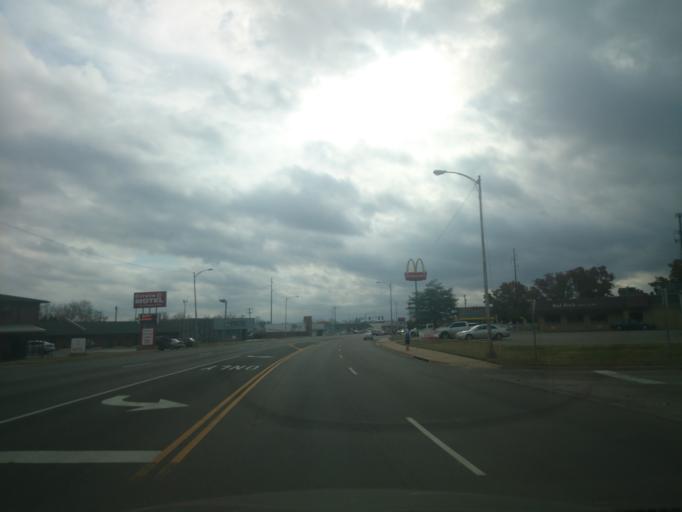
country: US
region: Oklahoma
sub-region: Payne County
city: Stillwater
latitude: 36.1323
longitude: -97.0605
